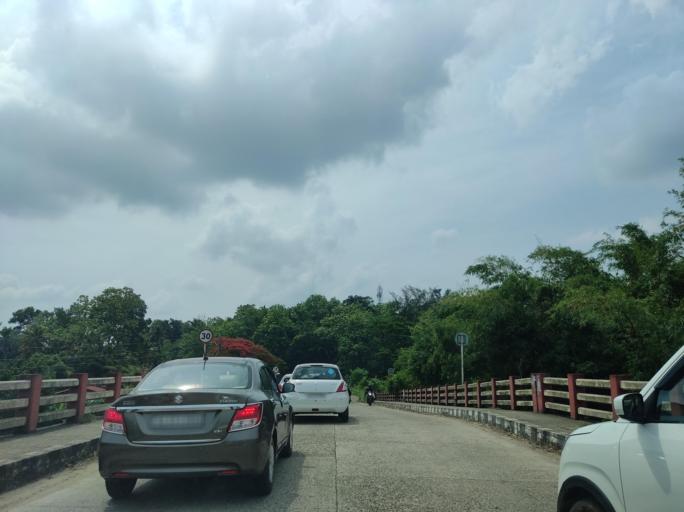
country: IN
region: Kerala
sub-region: Kottayam
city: Kottayam
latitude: 9.5625
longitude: 76.5117
